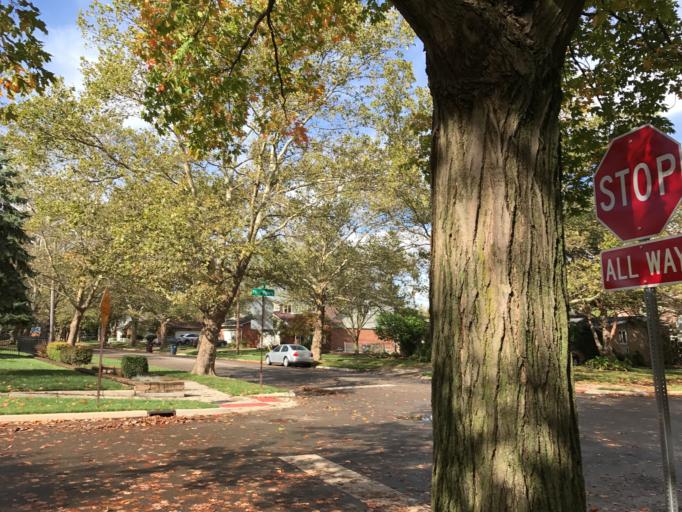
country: US
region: Michigan
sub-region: Washtenaw County
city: Ann Arbor
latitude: 42.2488
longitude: -83.7281
